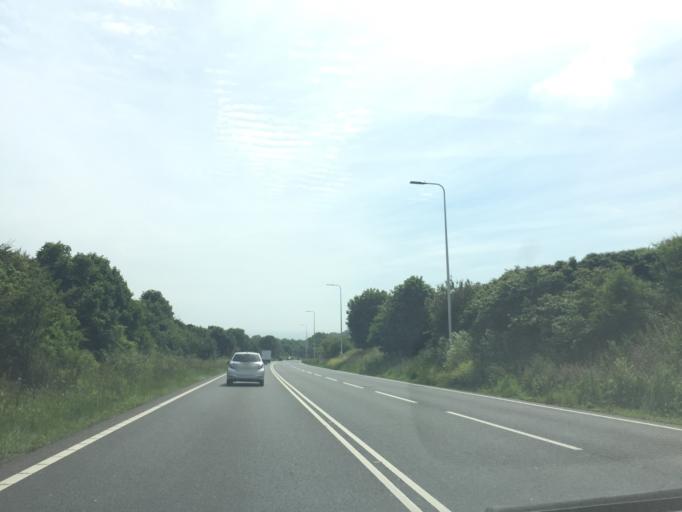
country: GB
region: England
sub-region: Kent
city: Dover
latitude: 51.1393
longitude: 1.3319
